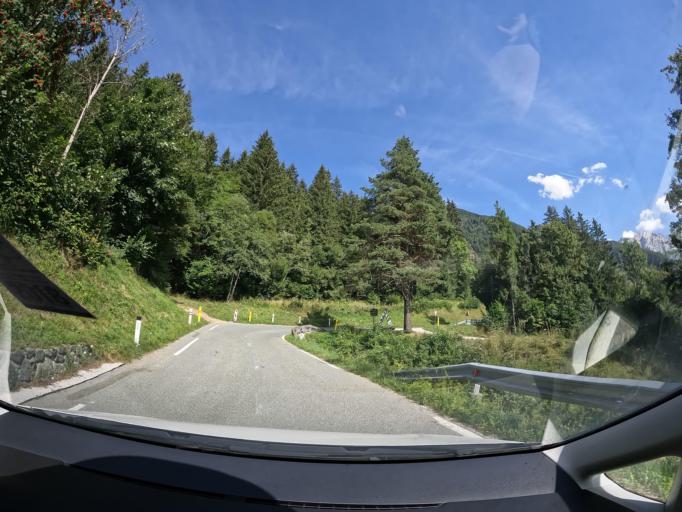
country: AT
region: Carinthia
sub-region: Politischer Bezirk Feldkirchen
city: Glanegg
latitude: 46.7360
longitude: 14.1845
